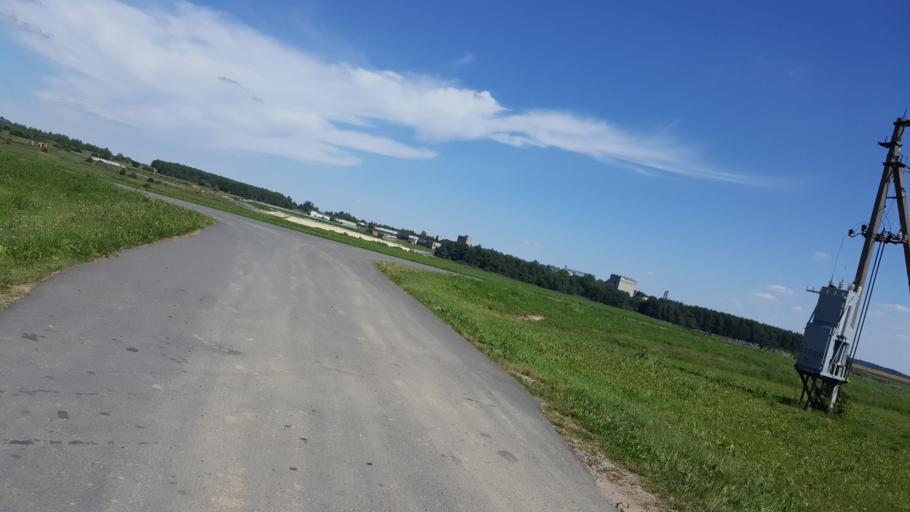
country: BY
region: Brest
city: Charnawchytsy
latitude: 52.2746
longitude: 23.5880
